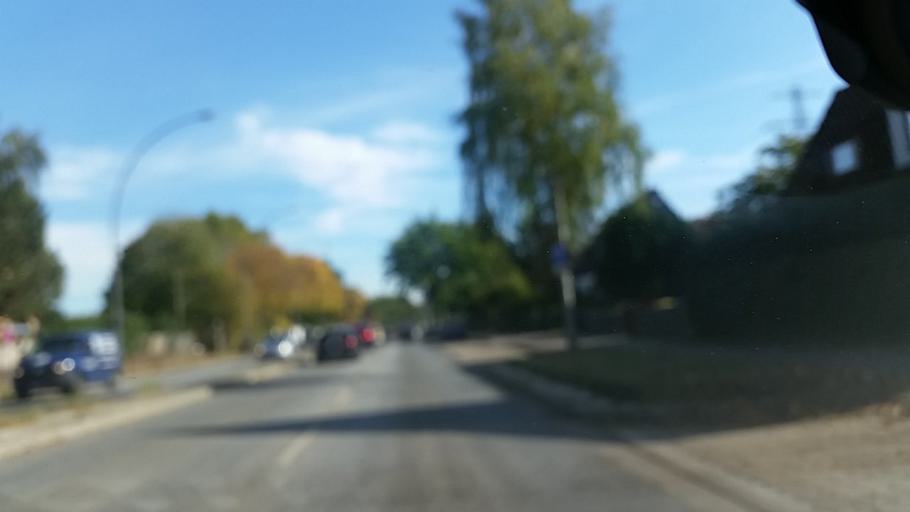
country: DE
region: Hamburg
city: Eidelstedt
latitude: 53.5930
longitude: 9.8954
